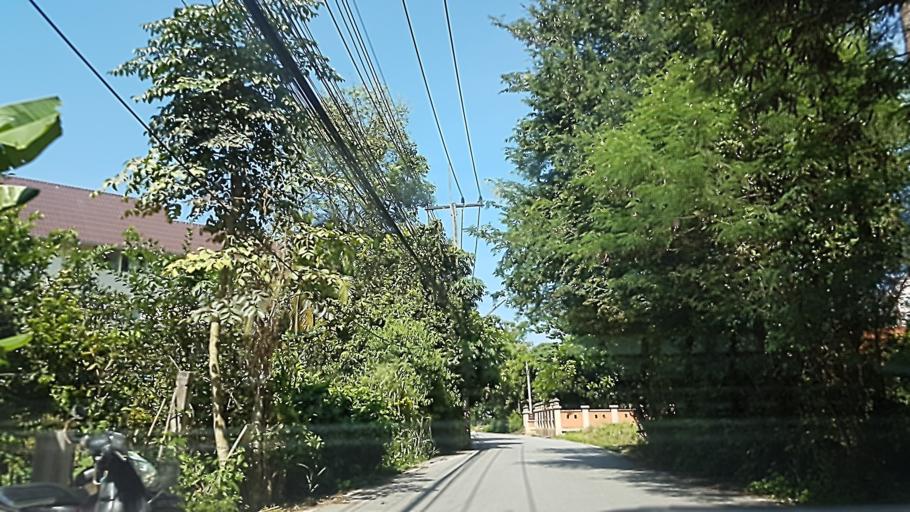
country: TH
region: Chiang Mai
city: Chiang Mai
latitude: 18.8199
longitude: 98.9574
